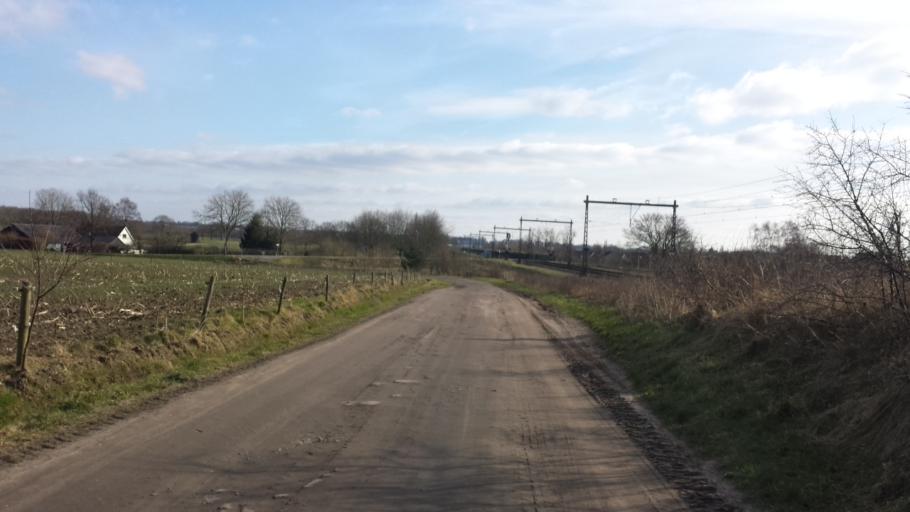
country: NL
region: Overijssel
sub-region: Gemeente Steenwijkerland
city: Tuk
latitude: 52.8025
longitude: 6.0945
